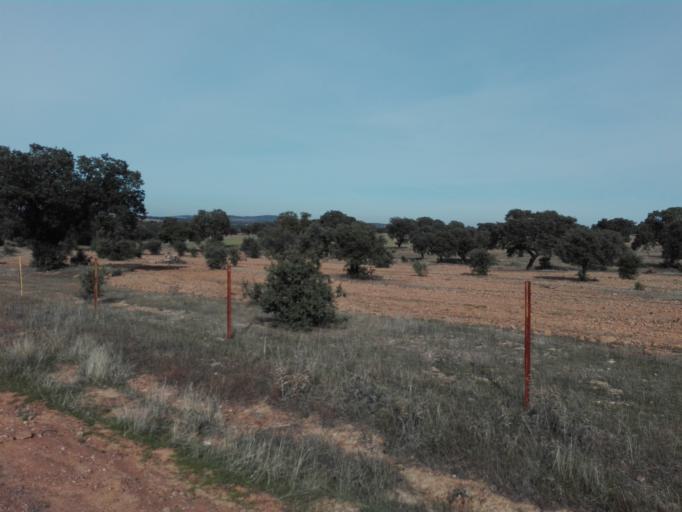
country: ES
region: Extremadura
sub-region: Provincia de Badajoz
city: Campillo de Llerena
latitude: 38.4585
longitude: -5.8746
